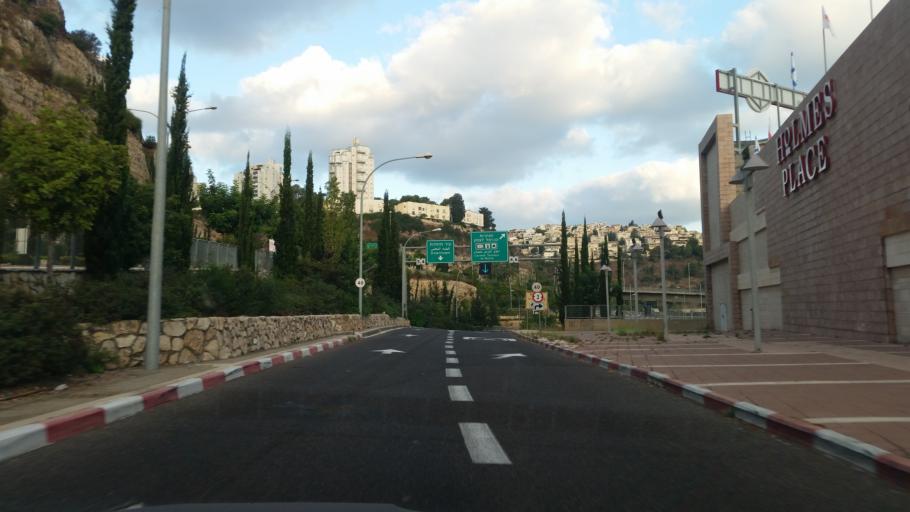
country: IL
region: Haifa
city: Haifa
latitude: 32.7893
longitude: 35.0069
